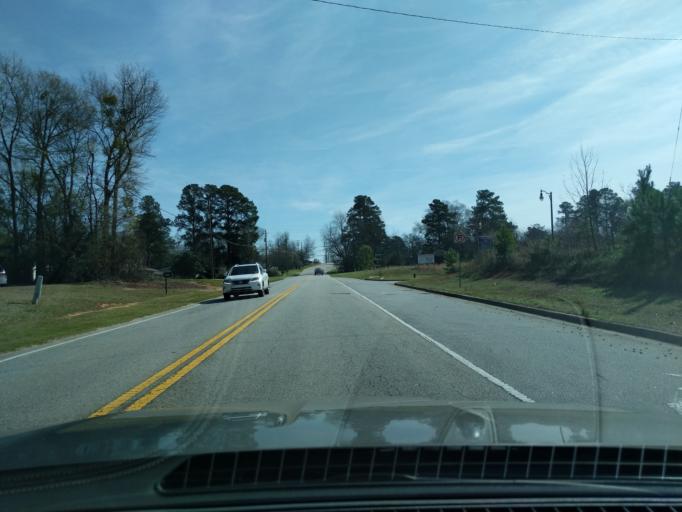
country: US
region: Georgia
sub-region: Columbia County
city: Evans
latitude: 33.5336
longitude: -82.1341
